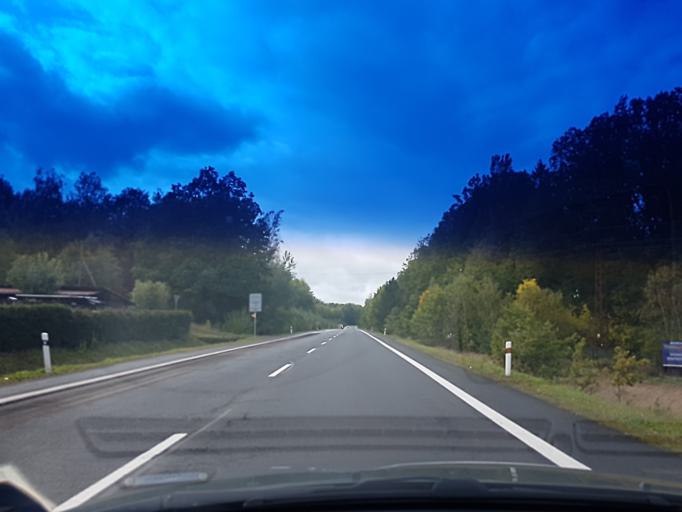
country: CZ
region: Karlovarsky
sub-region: Okres Cheb
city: Frantiskovy Lazne
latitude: 50.0814
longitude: 12.3215
